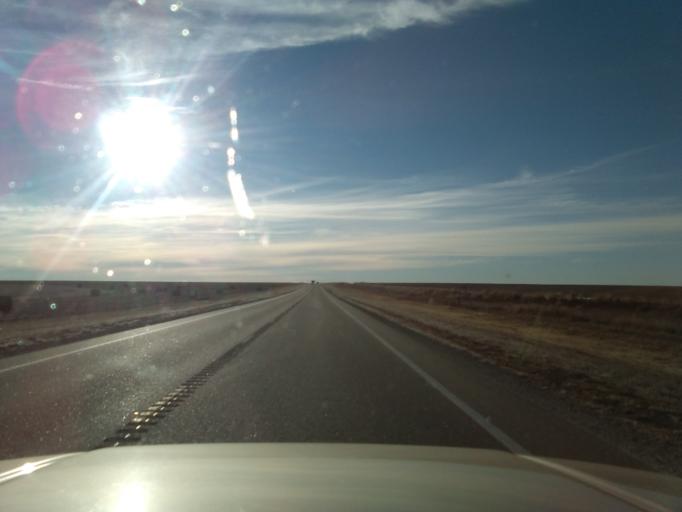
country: US
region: Kansas
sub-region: Sheridan County
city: Hoxie
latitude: 39.5317
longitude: -100.5968
